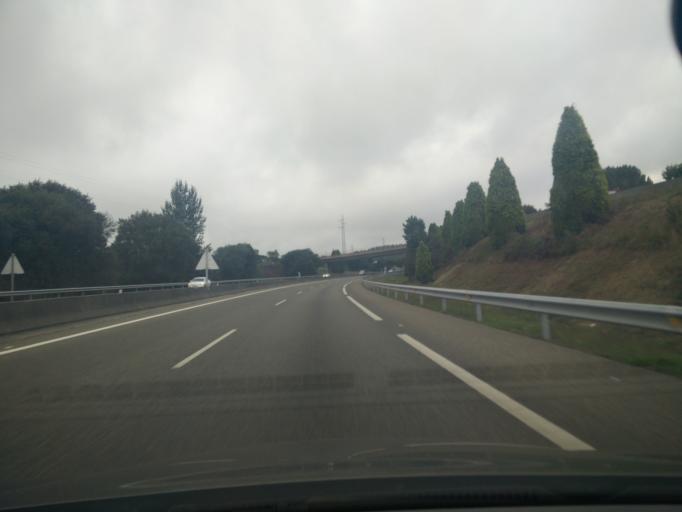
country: ES
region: Galicia
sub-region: Provincia da Coruna
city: Laracha
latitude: 43.2652
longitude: -8.5446
